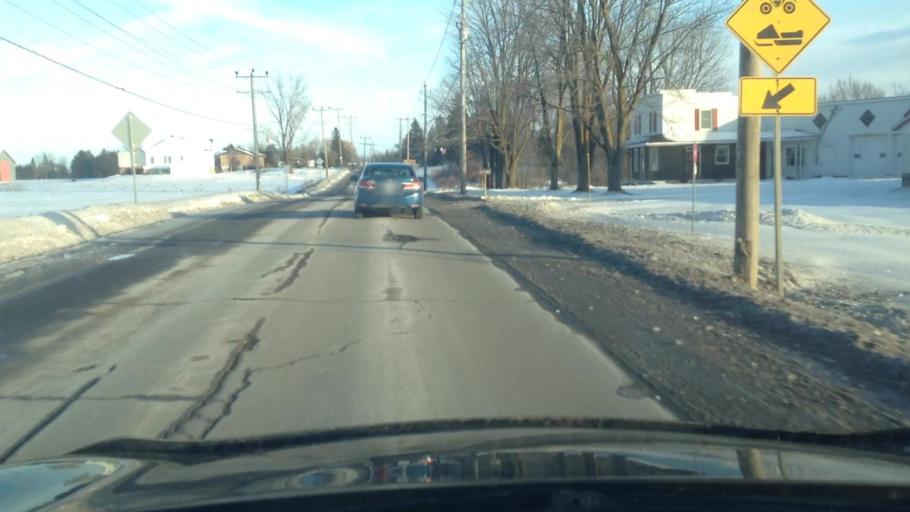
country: CA
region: Quebec
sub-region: Lanaudiere
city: Saint-Lin-Laurentides
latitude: 45.8521
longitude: -73.7705
